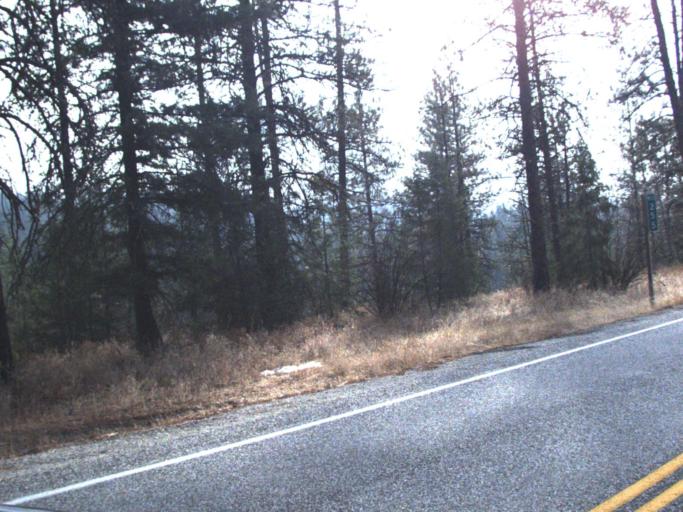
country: US
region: Washington
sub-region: Stevens County
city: Kettle Falls
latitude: 48.8015
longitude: -118.1611
